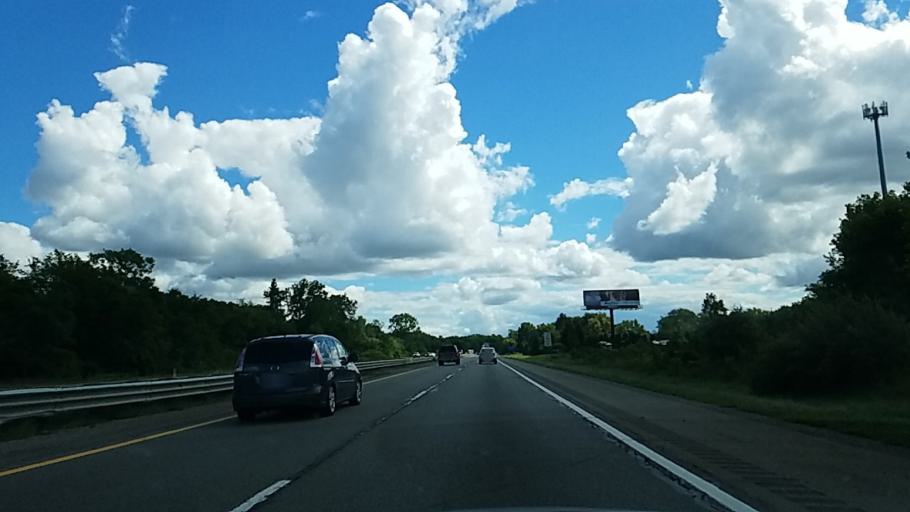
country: US
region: Michigan
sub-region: Livingston County
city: Whitmore Lake
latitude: 42.3745
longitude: -83.7542
